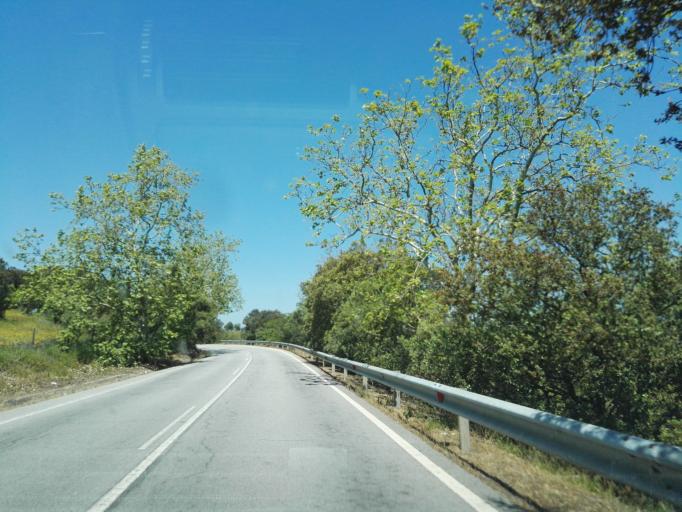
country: PT
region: Portalegre
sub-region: Elvas
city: Elvas
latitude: 38.9871
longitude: -7.2379
